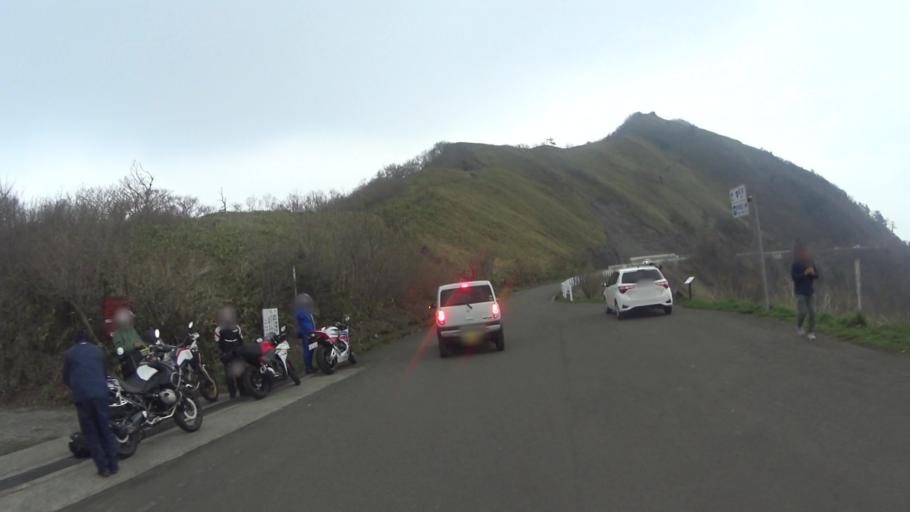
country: JP
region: Ehime
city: Saijo
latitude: 33.7837
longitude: 133.2299
